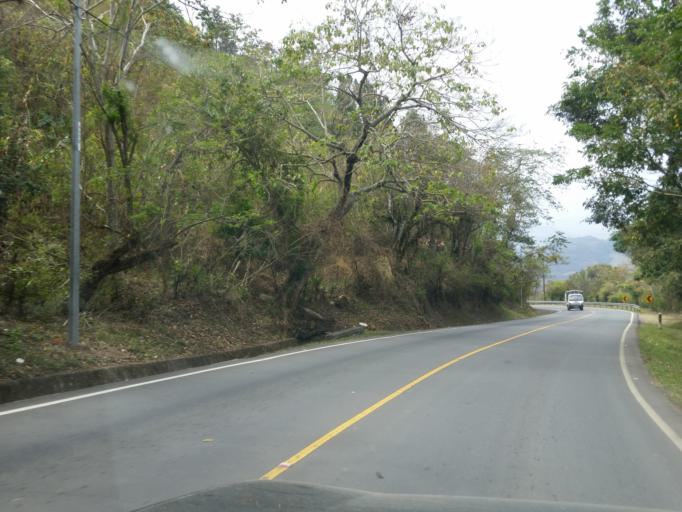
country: NI
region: Matagalpa
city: Matagalpa
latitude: 12.9696
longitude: -85.9195
